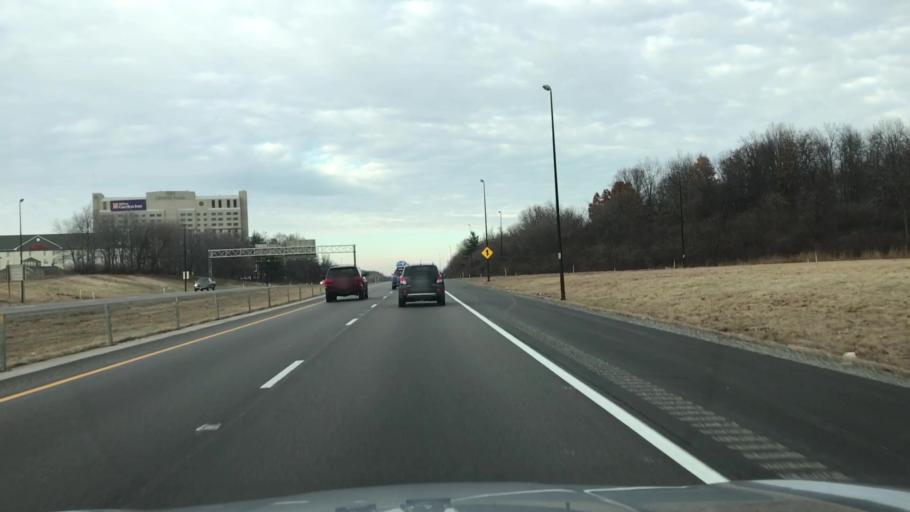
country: US
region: Illinois
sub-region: Sangamon County
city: Southern View
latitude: 39.7600
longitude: -89.6053
